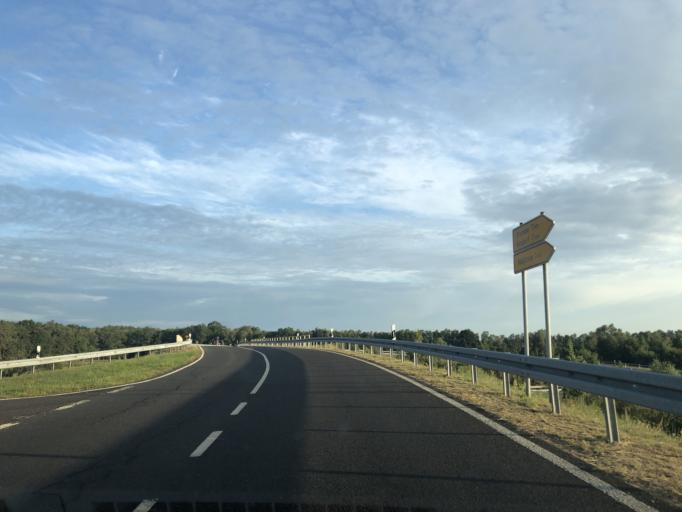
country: DE
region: Brandenburg
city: Mullrose
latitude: 52.2366
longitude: 14.3944
